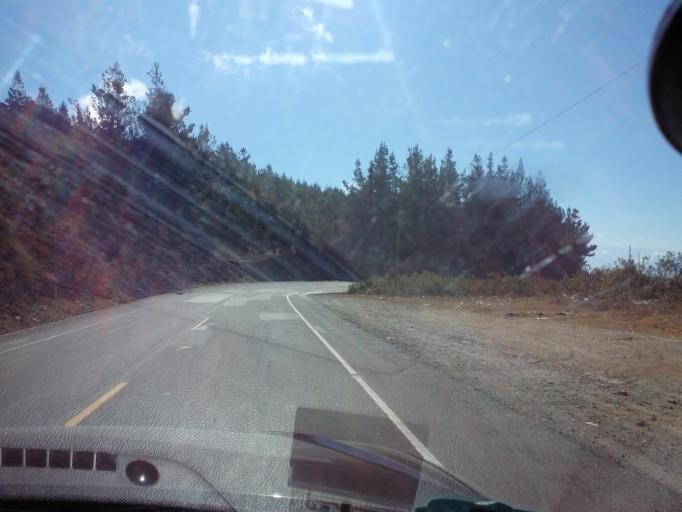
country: PE
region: Apurimac
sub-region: Provincia de Abancay
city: Cachora
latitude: -13.5557
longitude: -72.8163
